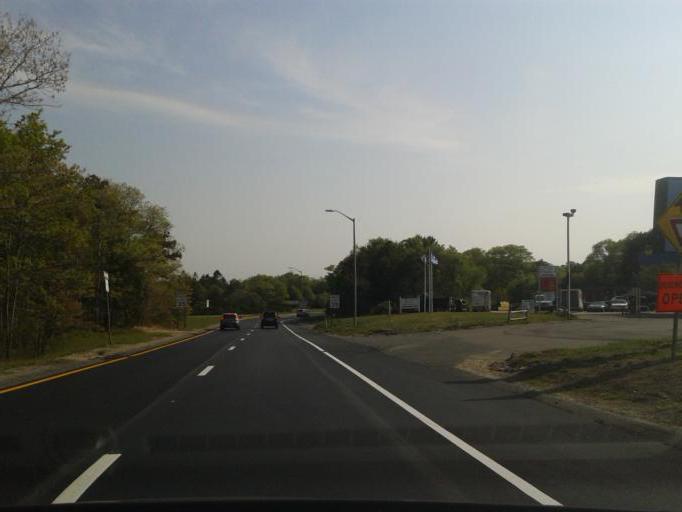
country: US
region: Massachusetts
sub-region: Barnstable County
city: Pocasset
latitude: 41.6877
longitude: -70.5909
